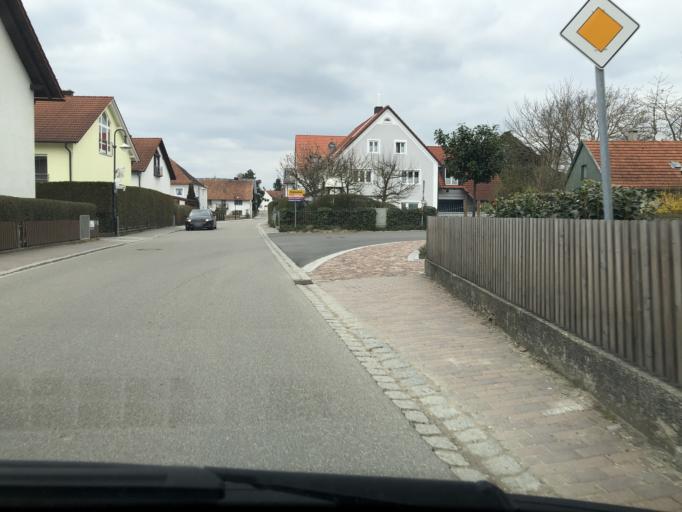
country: DE
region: Bavaria
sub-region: Upper Bavaria
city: Wolfersdorf
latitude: 48.4786
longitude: 11.7089
